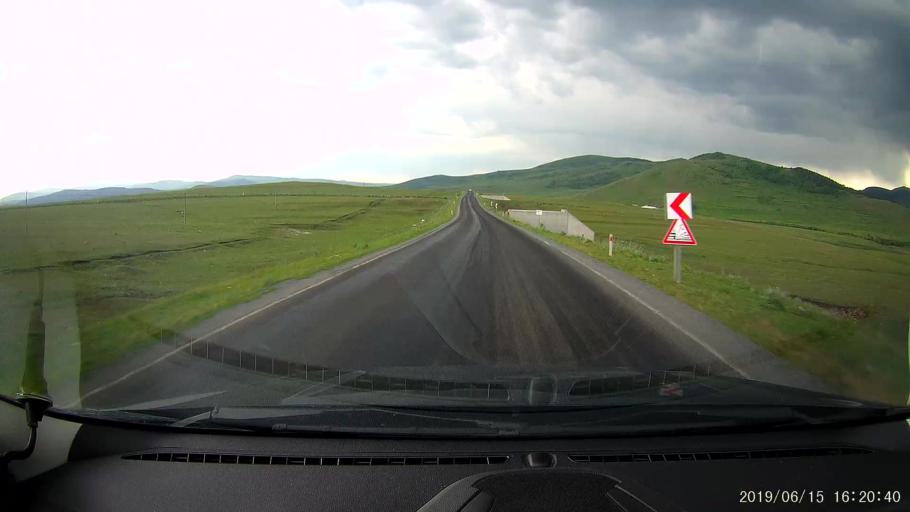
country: TR
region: Ardahan
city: Hanak
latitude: 41.2103
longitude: 42.8468
